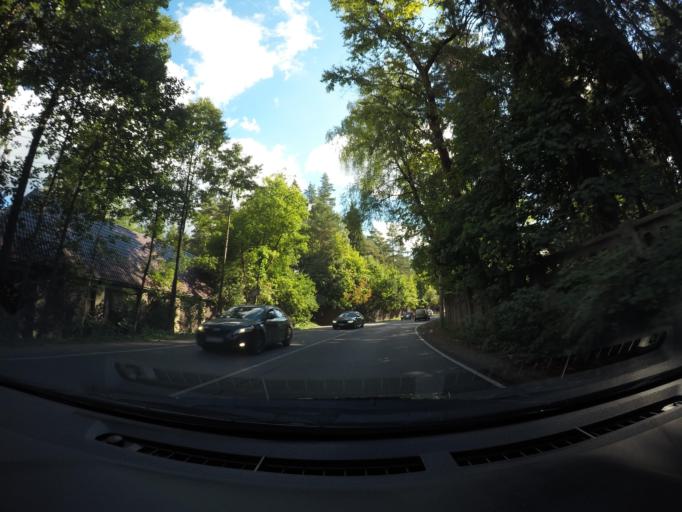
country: RU
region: Moskovskaya
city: Kratovo
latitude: 55.6038
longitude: 38.1545
